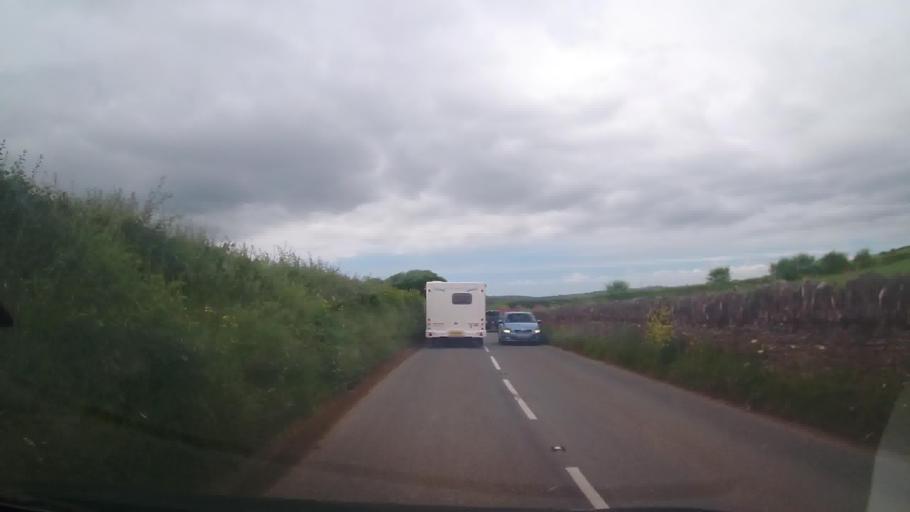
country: GB
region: England
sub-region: Devon
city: Kingsbridge
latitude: 50.2700
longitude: -3.7424
